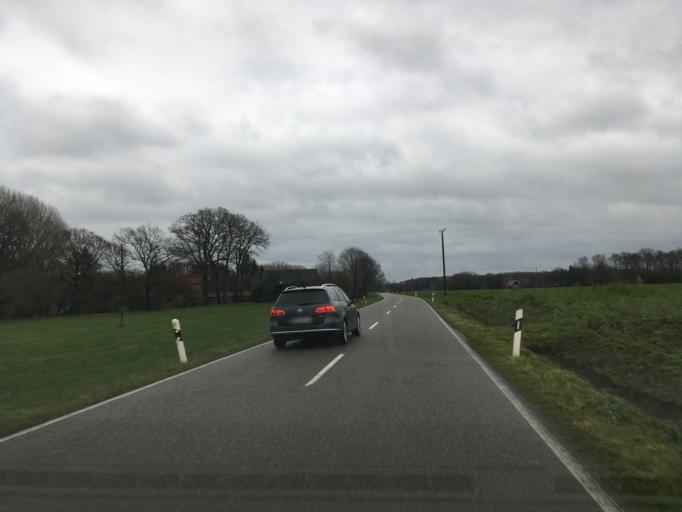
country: DE
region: North Rhine-Westphalia
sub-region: Regierungsbezirk Munster
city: Legden
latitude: 52.0476
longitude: 7.1602
